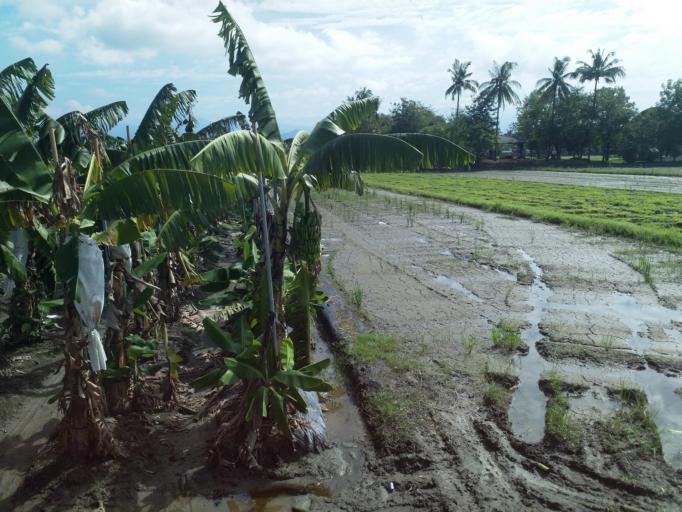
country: TW
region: Taiwan
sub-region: Pingtung
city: Pingtung
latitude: 22.8986
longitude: 120.5178
